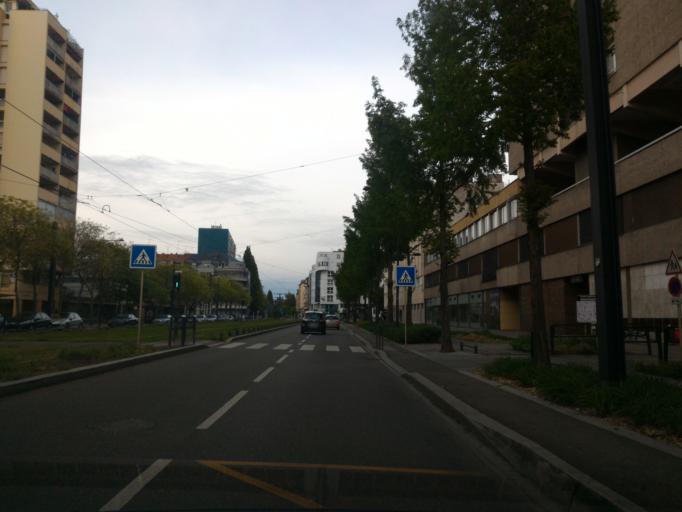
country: FR
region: Alsace
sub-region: Departement du Haut-Rhin
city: Mulhouse
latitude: 47.7505
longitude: 7.3422
